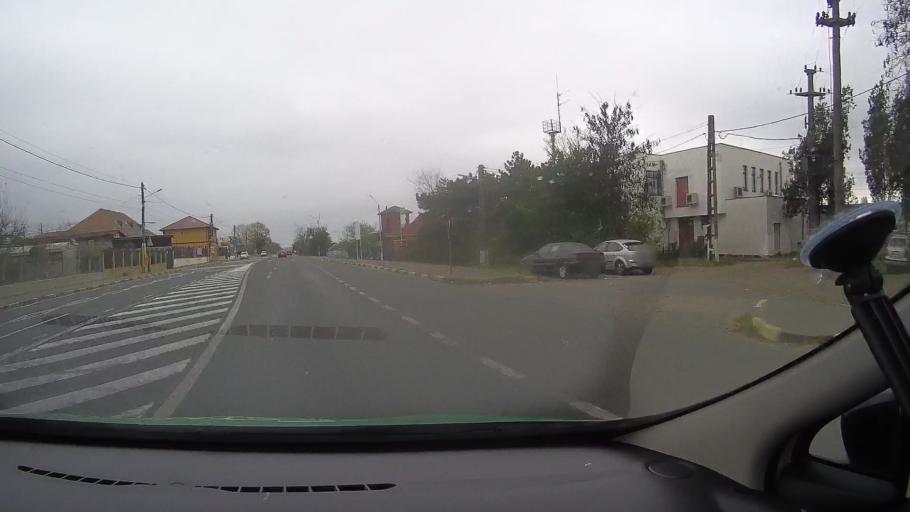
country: RO
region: Constanta
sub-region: Oras Murfatlar
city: Murfatlar
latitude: 44.1722
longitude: 28.4178
